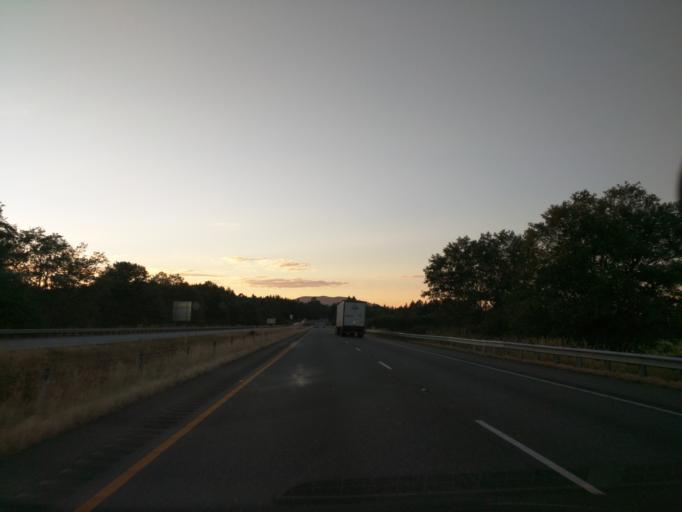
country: US
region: Washington
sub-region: Skagit County
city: Burlington
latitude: 48.5201
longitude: -122.3466
